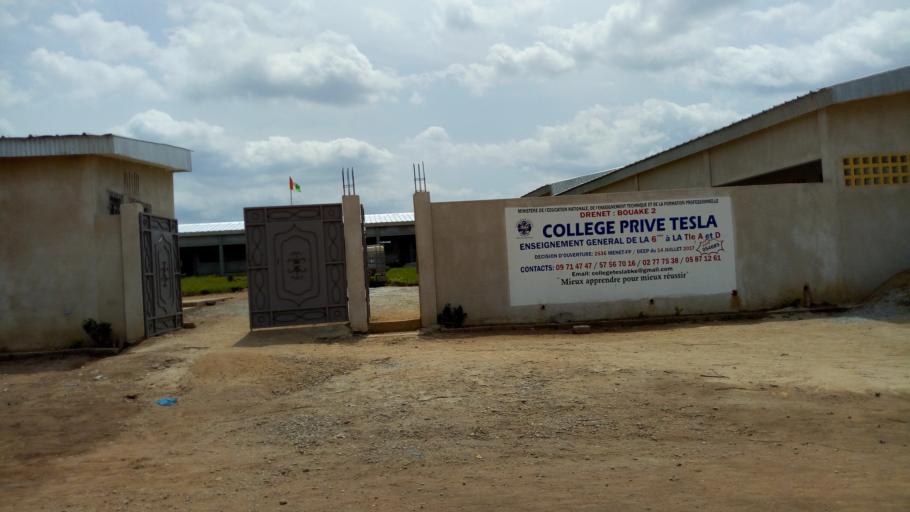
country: CI
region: Vallee du Bandama
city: Bouake
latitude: 7.6612
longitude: -5.0440
